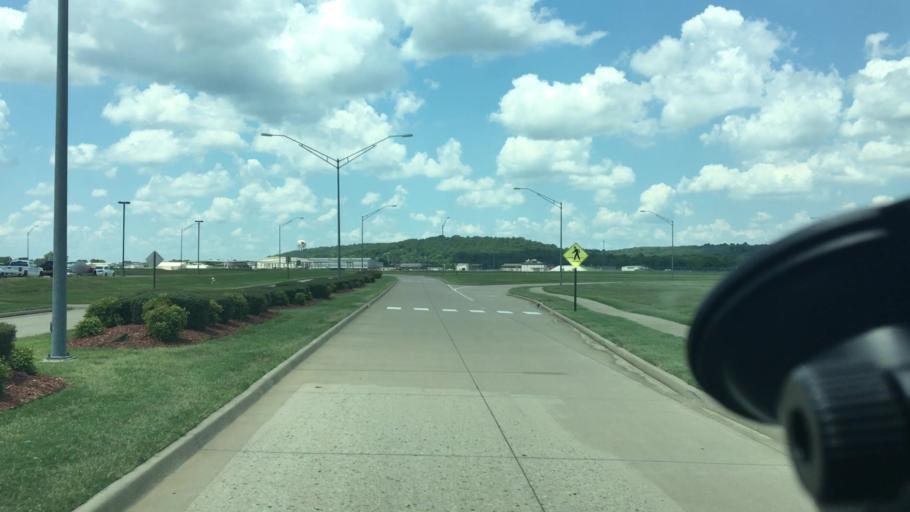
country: US
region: Arkansas
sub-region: Sebastian County
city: Fort Smith
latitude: 35.3428
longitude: -94.3585
